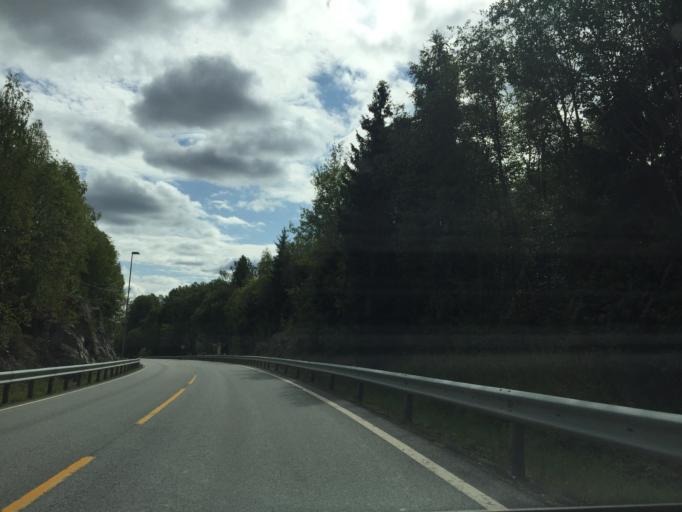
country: NO
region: Ostfold
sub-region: Hobol
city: Elvestad
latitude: 59.6329
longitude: 10.9360
